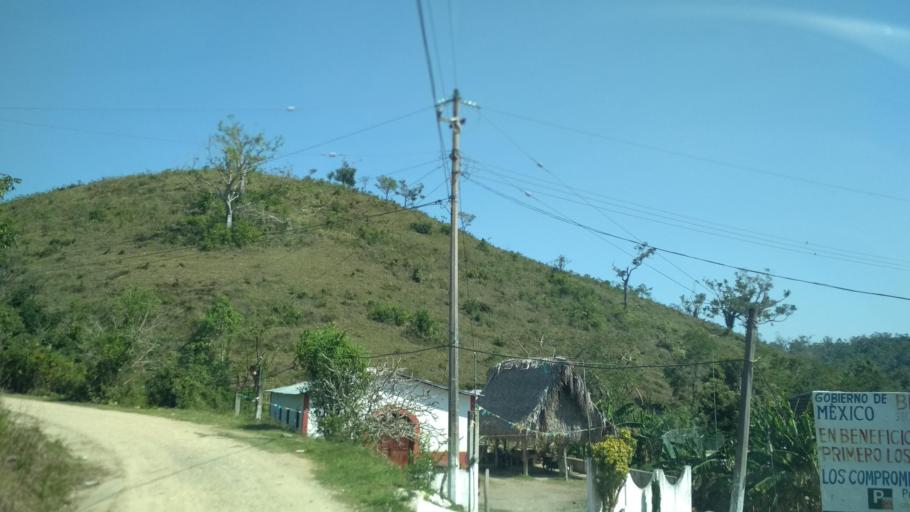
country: MX
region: Veracruz
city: Gutierrez Zamora
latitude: 20.4882
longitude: -97.1598
